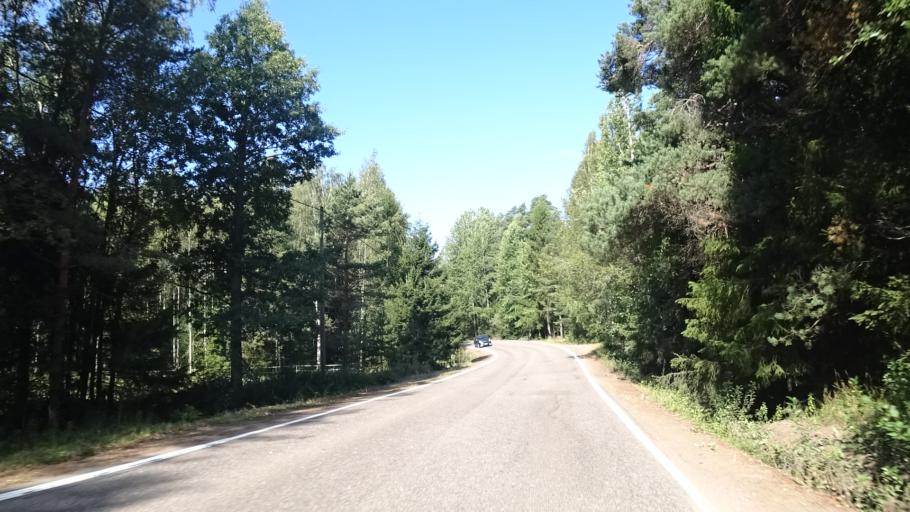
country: FI
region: Kymenlaakso
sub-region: Kotka-Hamina
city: Hamina
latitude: 60.5540
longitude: 27.2422
